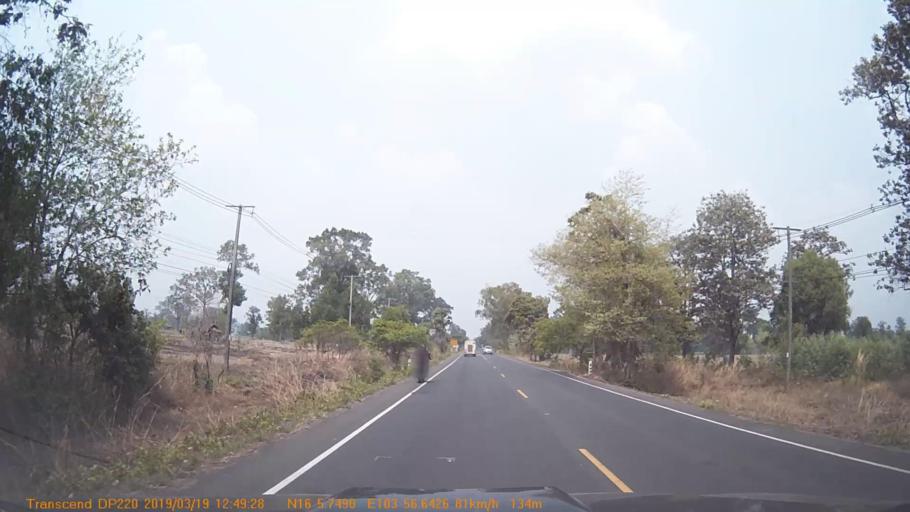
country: TH
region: Roi Et
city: Selaphum
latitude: 16.0962
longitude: 103.9441
